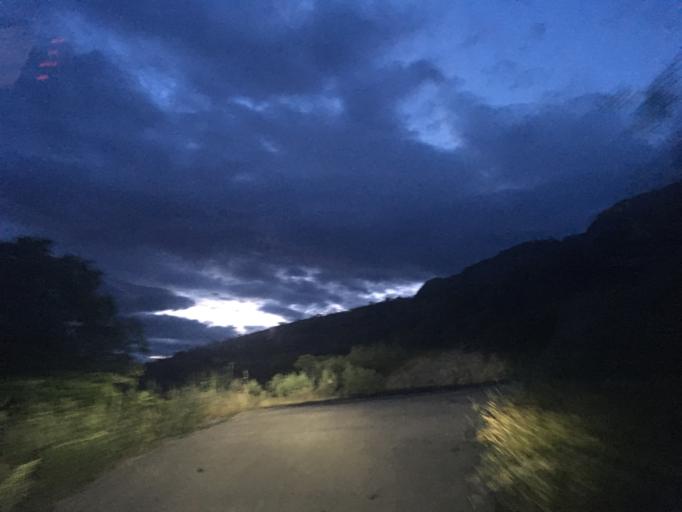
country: HR
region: Splitsko-Dalmatinska
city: Srinjine
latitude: 43.4639
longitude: 16.5946
